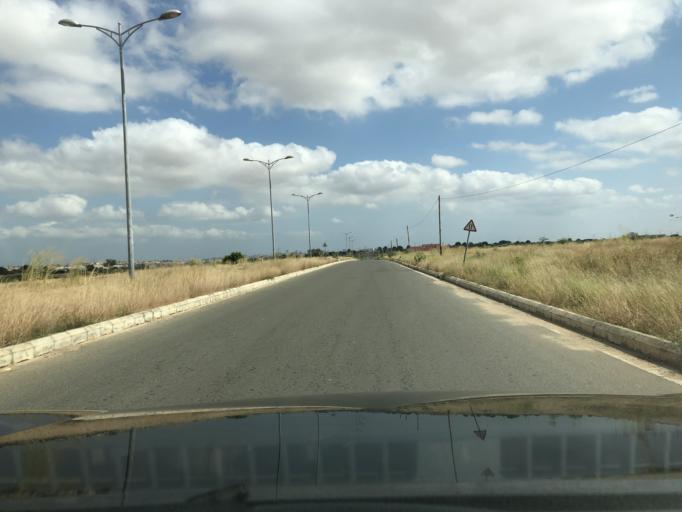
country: AO
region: Luanda
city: Luanda
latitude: -8.9638
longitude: 13.2445
